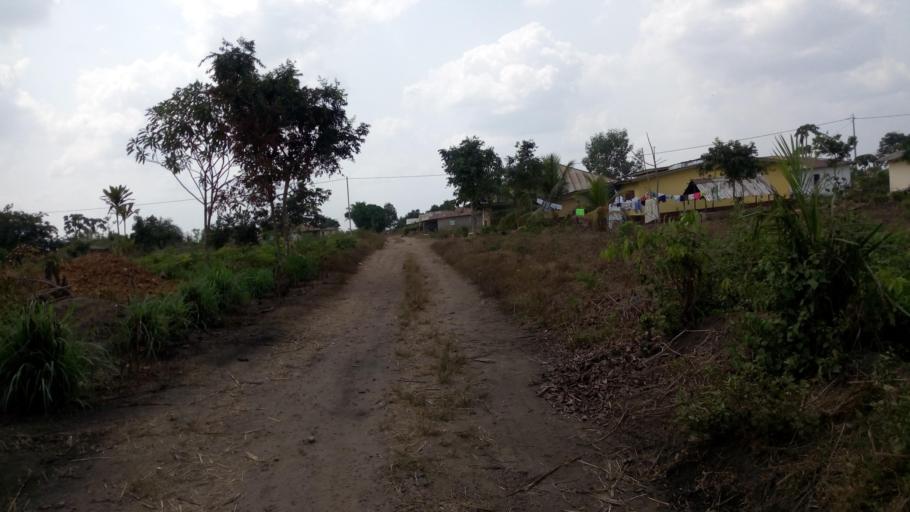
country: SL
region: Southern Province
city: Mogbwemo
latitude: 7.7914
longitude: -12.3049
